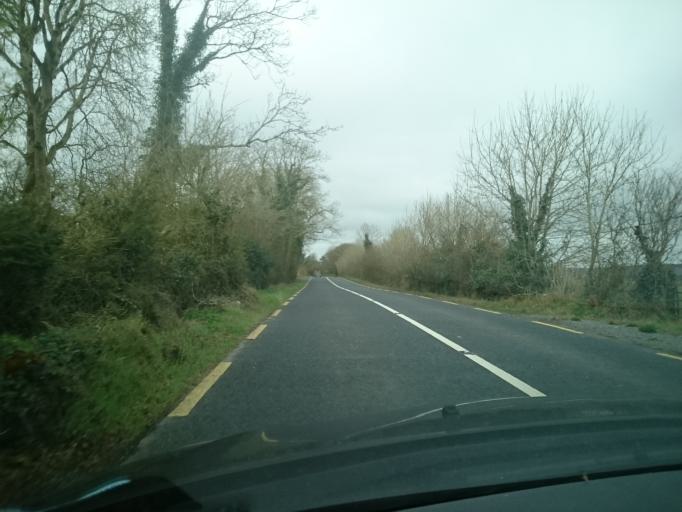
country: IE
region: Connaught
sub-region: Maigh Eo
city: Claremorris
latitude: 53.7715
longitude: -9.0602
